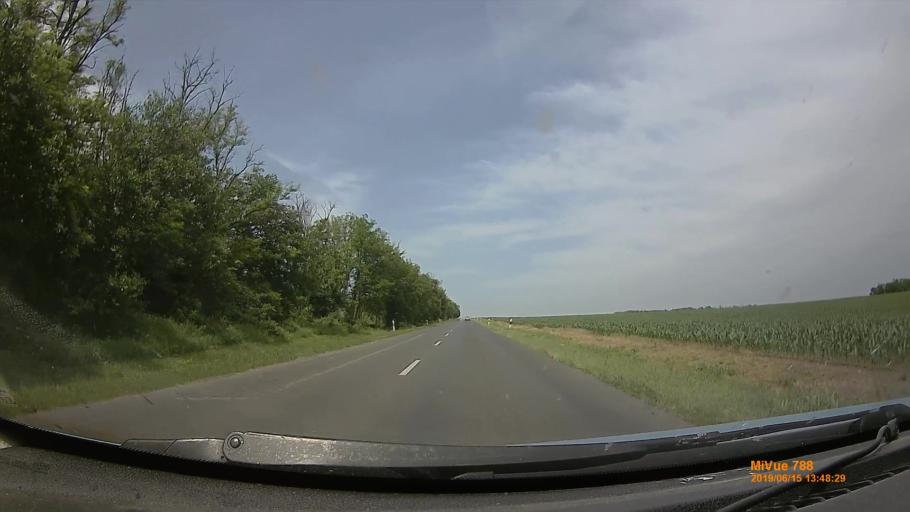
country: HU
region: Tolna
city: Iregszemcse
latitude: 46.7165
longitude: 18.1735
